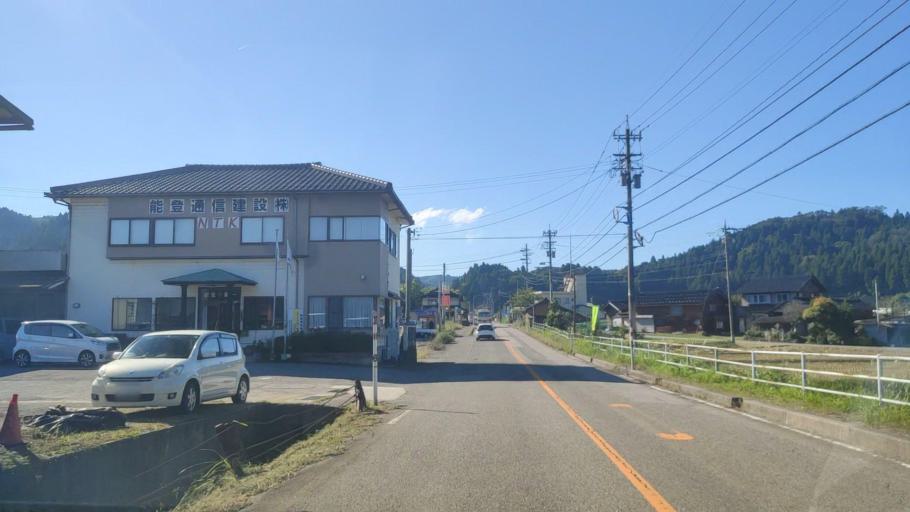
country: JP
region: Ishikawa
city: Nanao
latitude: 37.2808
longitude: 137.0440
